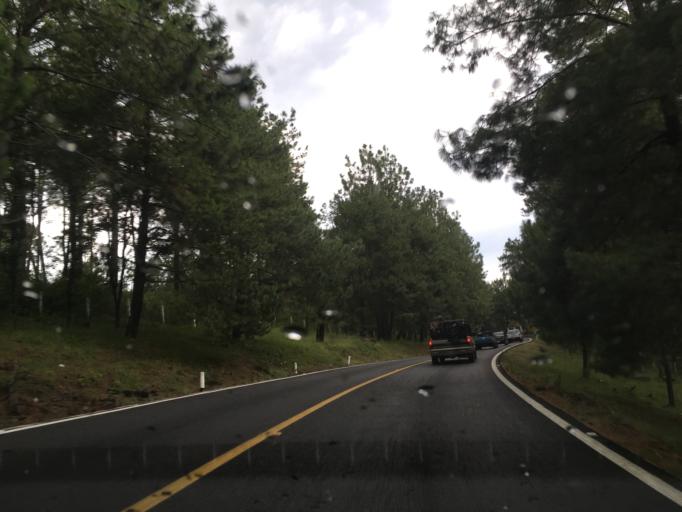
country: MX
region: Michoacan
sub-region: Patzcuaro
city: Santa Maria Huiramangaro (San Juan Tumbio)
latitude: 19.4980
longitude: -101.7524
